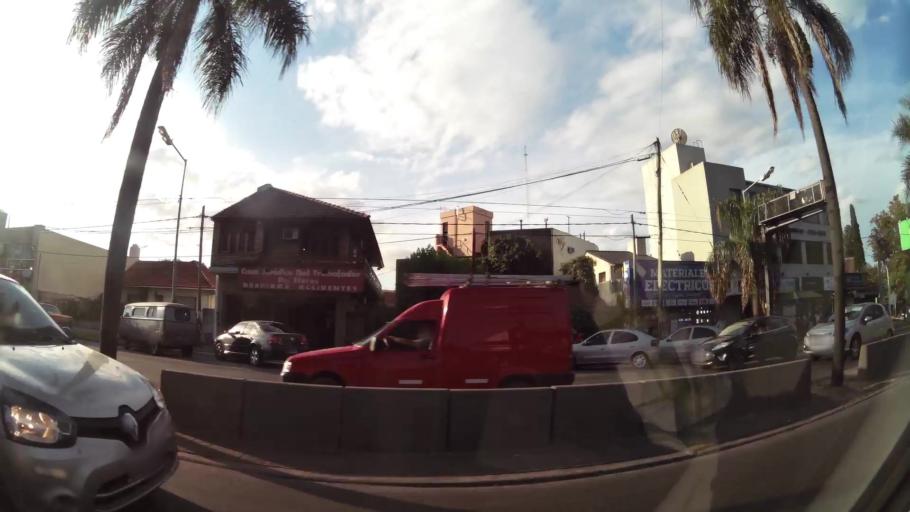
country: AR
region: Buenos Aires
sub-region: Partido de Tigre
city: Tigre
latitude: -34.4565
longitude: -58.6273
